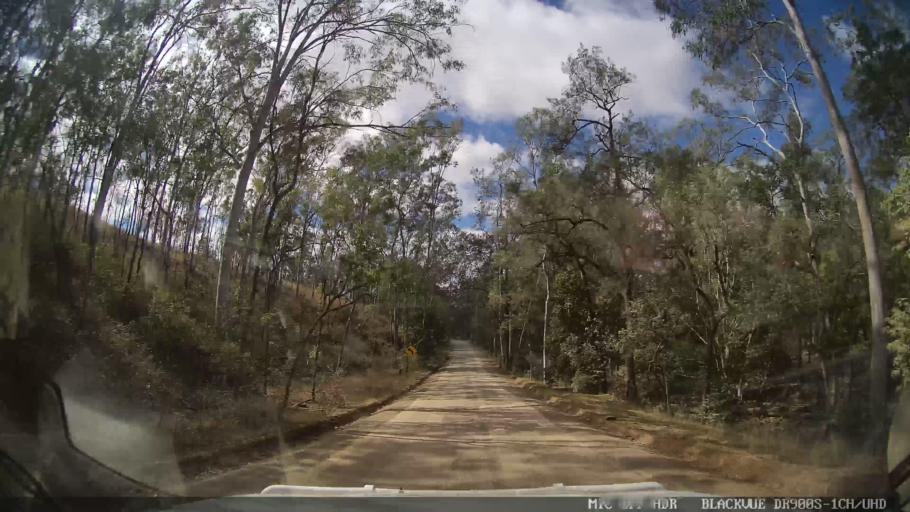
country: AU
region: Queensland
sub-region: Gladstone
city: Toolooa
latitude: -24.5514
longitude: 151.3385
